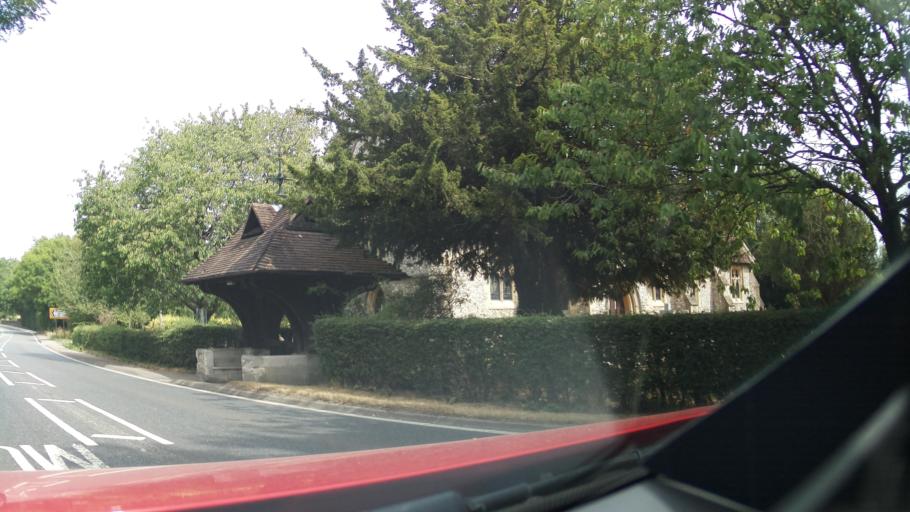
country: GB
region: England
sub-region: Surrey
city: Salfords
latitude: 51.2073
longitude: -0.1992
